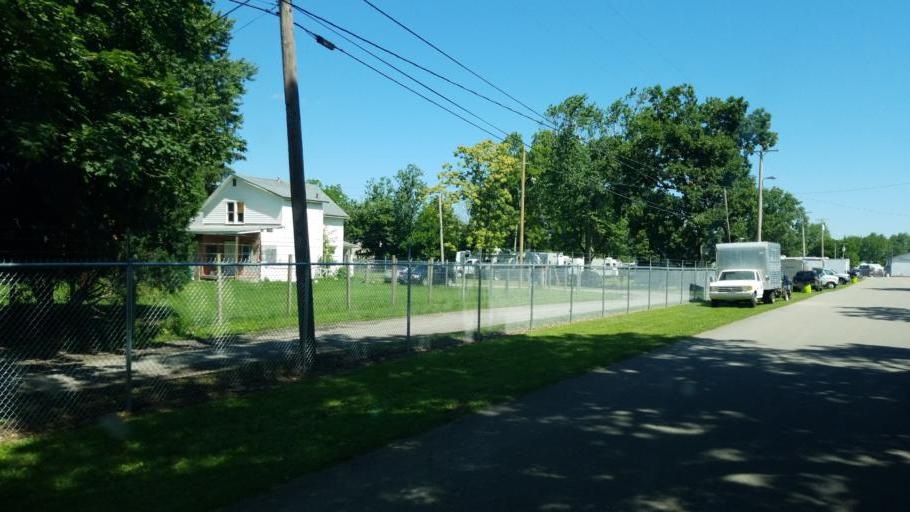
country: US
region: Ohio
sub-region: Marion County
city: Marion
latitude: 40.6023
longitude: -83.1264
